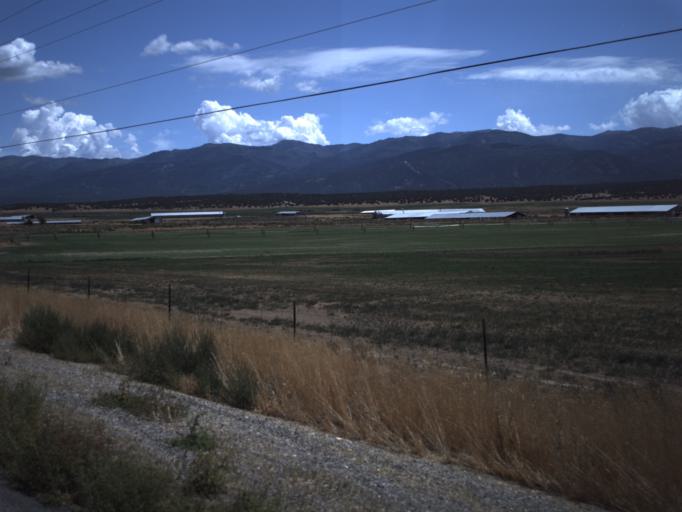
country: US
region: Utah
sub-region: Sanpete County
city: Moroni
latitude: 39.4770
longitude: -111.5523
